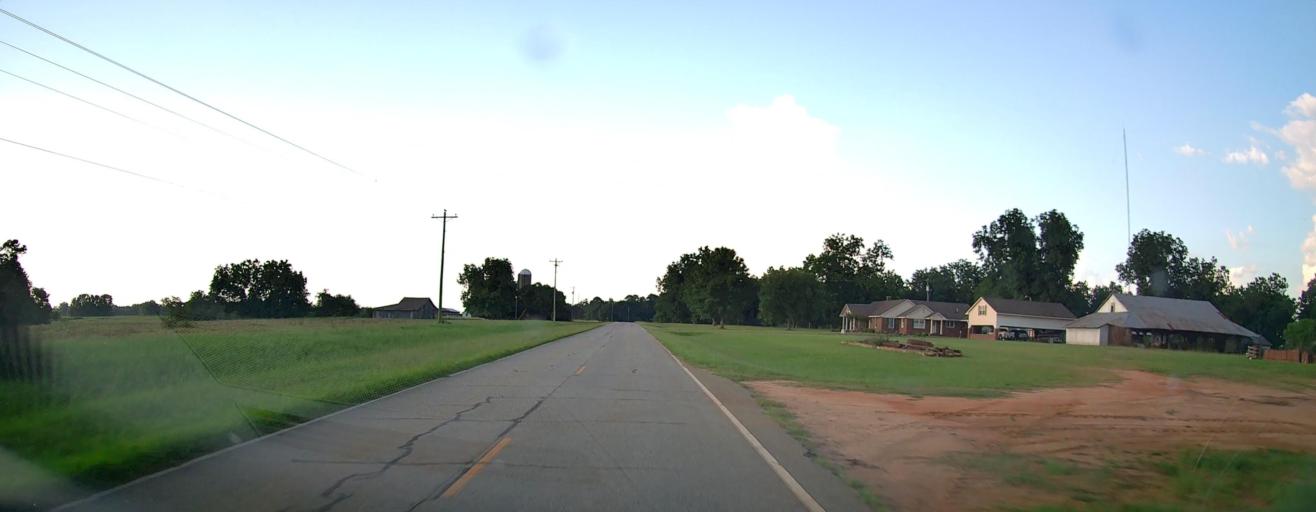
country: US
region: Georgia
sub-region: Peach County
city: Fort Valley
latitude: 32.6079
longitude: -83.8341
